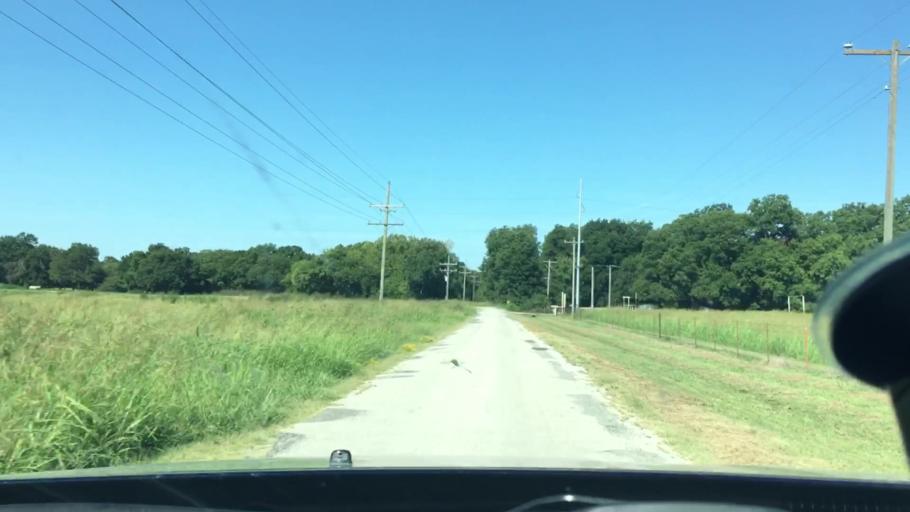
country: US
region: Oklahoma
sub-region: Pontotoc County
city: Ada
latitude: 34.7236
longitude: -96.6401
